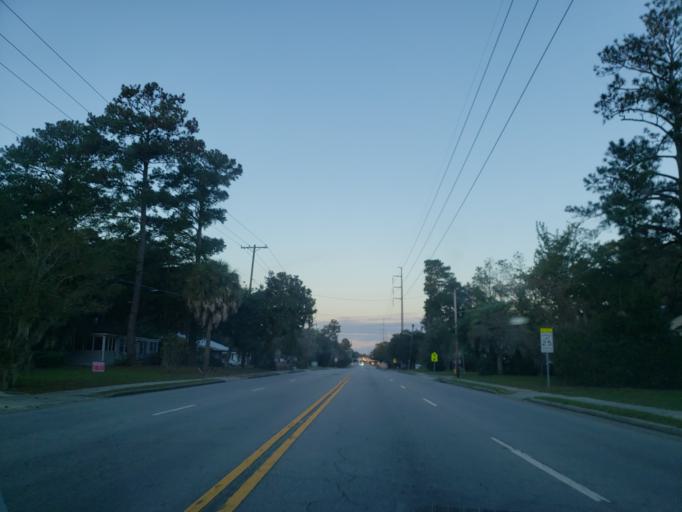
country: US
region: Georgia
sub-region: Chatham County
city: Thunderbolt
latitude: 32.0208
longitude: -81.0808
